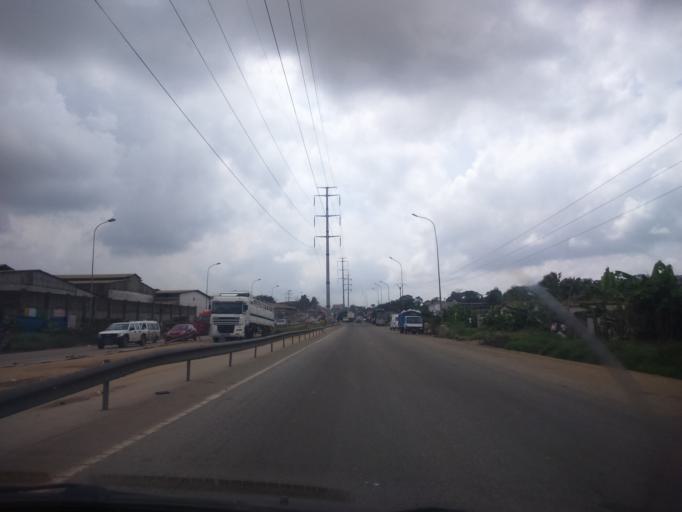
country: CI
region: Lagunes
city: Abobo
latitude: 5.3724
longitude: -4.0786
